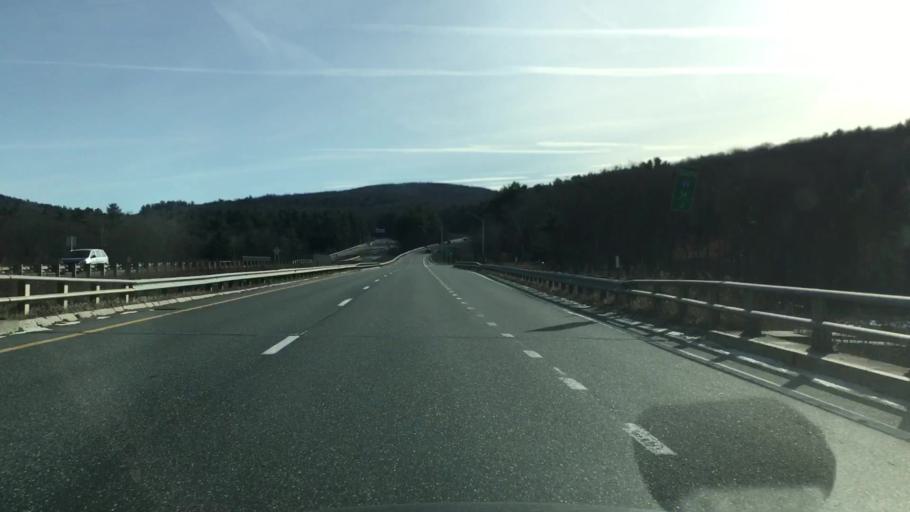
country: US
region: New Hampshire
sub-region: Grafton County
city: Lebanon
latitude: 43.6365
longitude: -72.2127
